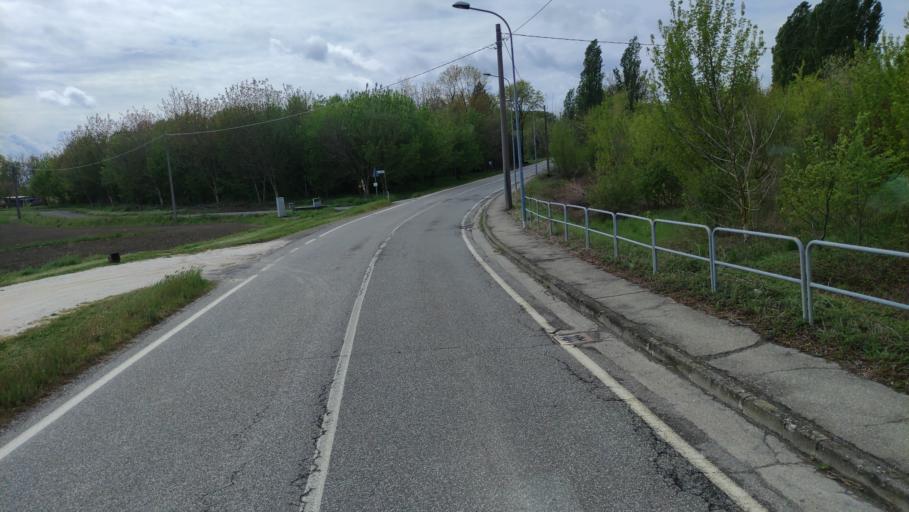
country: IT
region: Emilia-Romagna
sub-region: Provincia di Parma
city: Colorno
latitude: 44.9308
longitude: 10.3690
